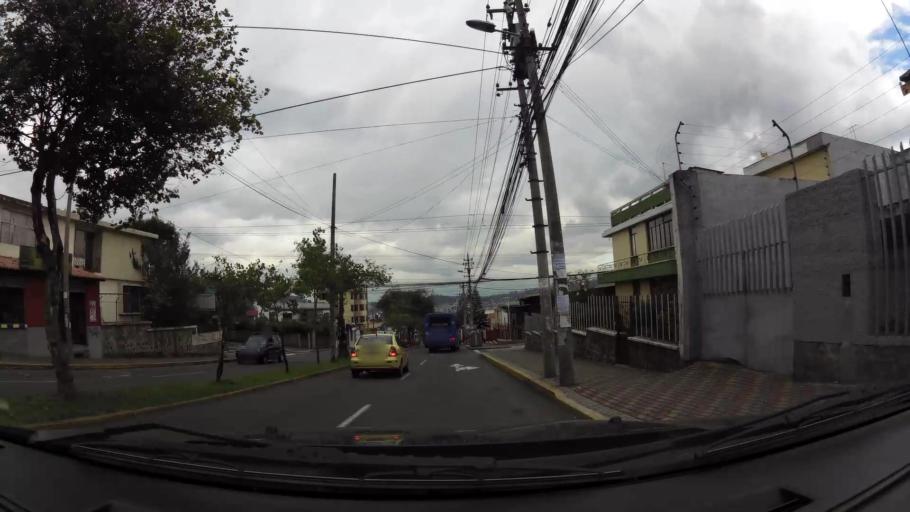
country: EC
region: Pichincha
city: Quito
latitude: -0.1952
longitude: -78.5080
